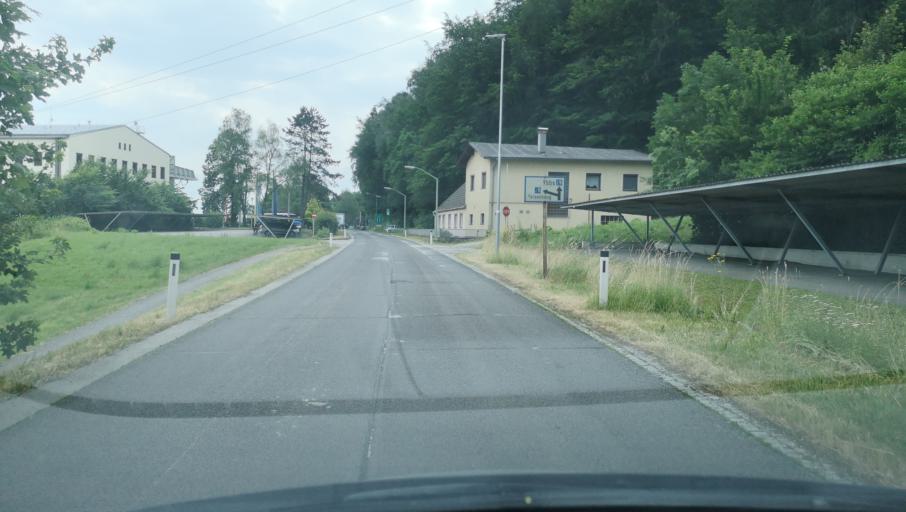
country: AT
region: Lower Austria
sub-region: Politischer Bezirk Melk
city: Ybbs an der Donau
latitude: 48.1889
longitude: 15.0647
